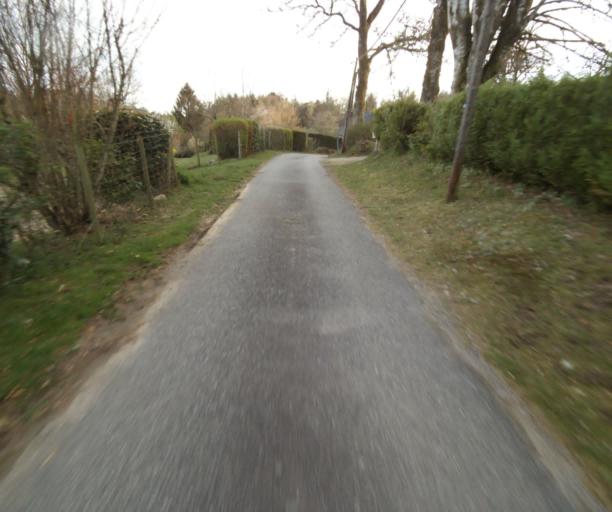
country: FR
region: Limousin
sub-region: Departement de la Correze
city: Argentat
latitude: 45.2461
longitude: 1.9602
